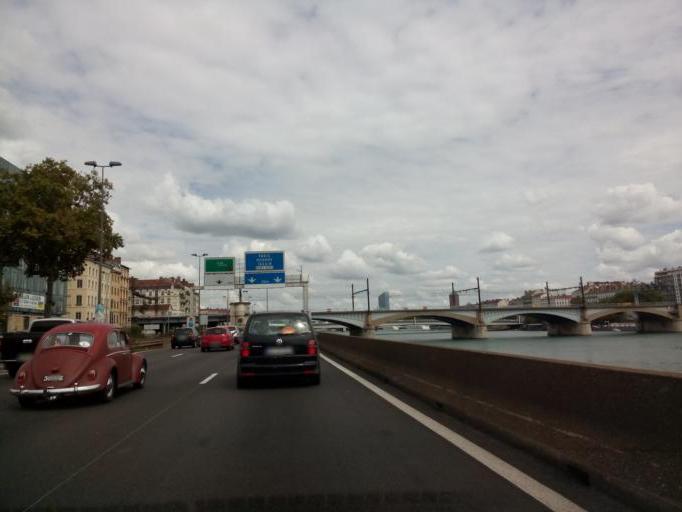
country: FR
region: Rhone-Alpes
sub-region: Departement du Rhone
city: Lyon
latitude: 45.7453
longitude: 4.8280
